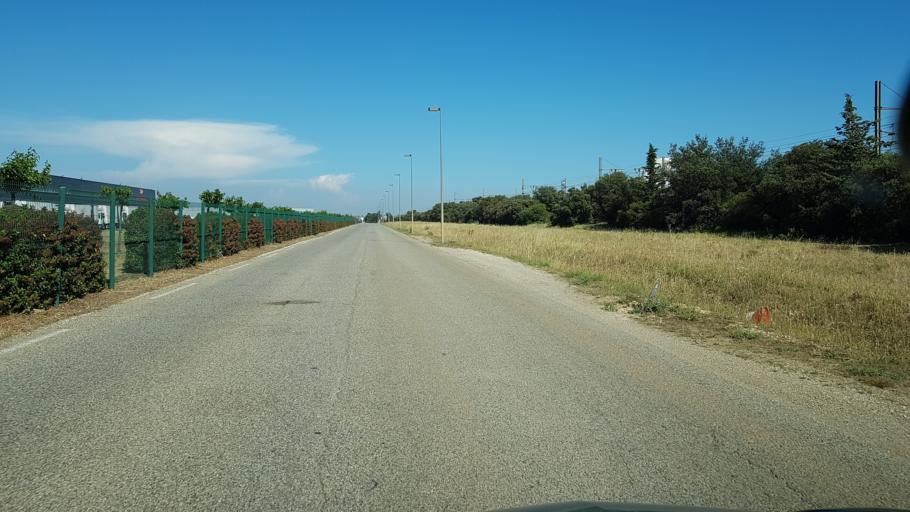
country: FR
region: Provence-Alpes-Cote d'Azur
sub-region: Departement des Bouches-du-Rhone
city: Saint-Martin-de-Crau
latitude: 43.6260
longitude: 4.7857
